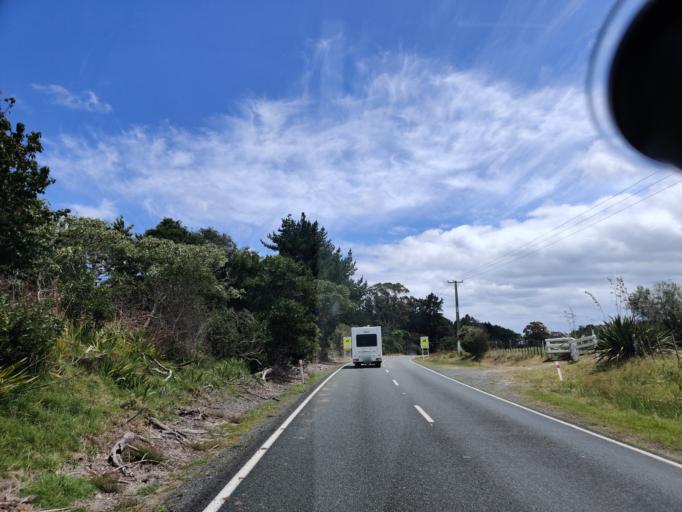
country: NZ
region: Northland
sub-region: Far North District
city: Kaitaia
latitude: -34.7461
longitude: 173.0487
